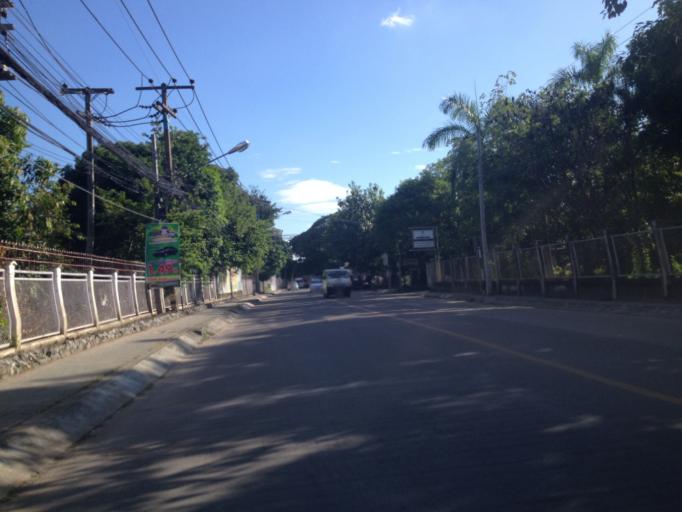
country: TH
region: Chiang Mai
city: Chiang Mai
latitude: 18.7936
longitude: 98.9708
